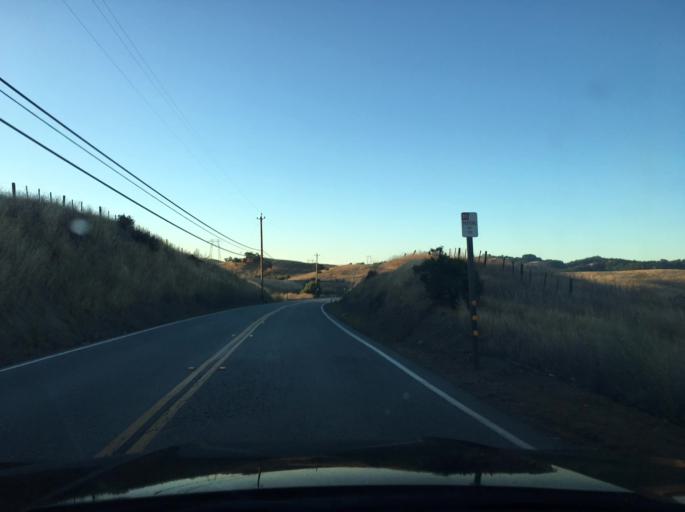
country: US
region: California
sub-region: Santa Clara County
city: Morgan Hill
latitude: 37.1844
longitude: -121.7647
